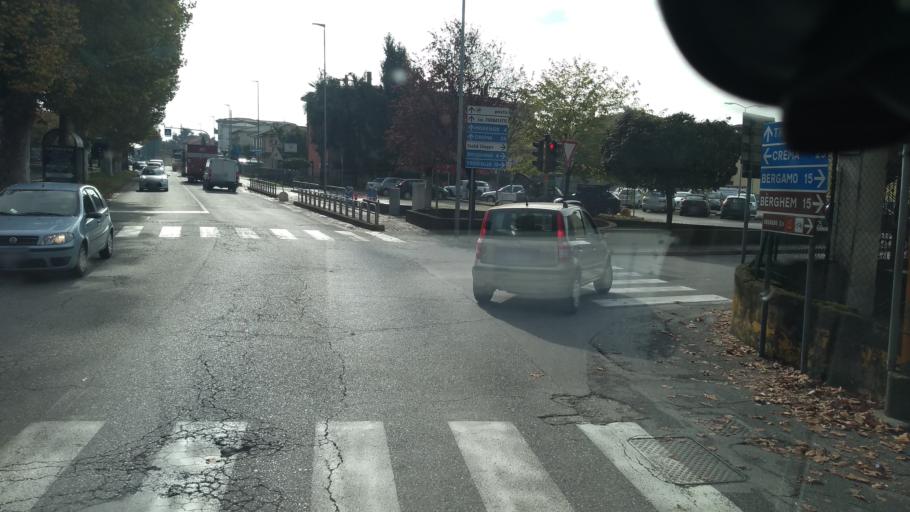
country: IT
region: Lombardy
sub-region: Provincia di Bergamo
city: Cologno al Serio
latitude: 45.5784
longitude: 9.7038
